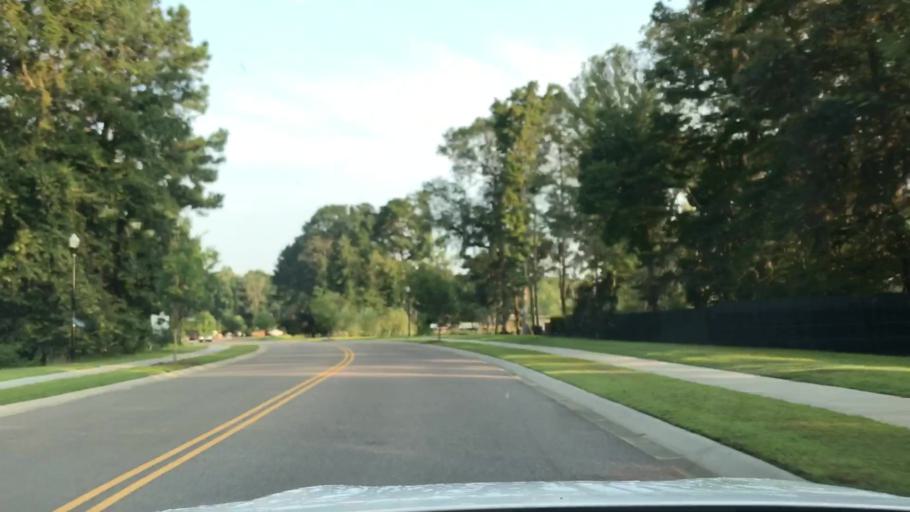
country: US
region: South Carolina
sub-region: Charleston County
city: Shell Point
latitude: 32.8256
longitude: -80.0959
